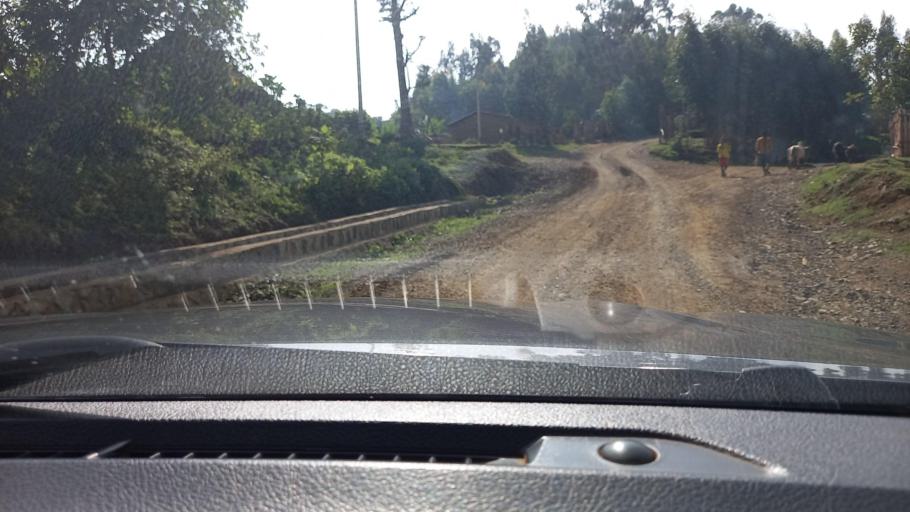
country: ET
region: Southern Nations, Nationalities, and People's Region
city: Mizan Teferi
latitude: 6.1629
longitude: 35.5945
